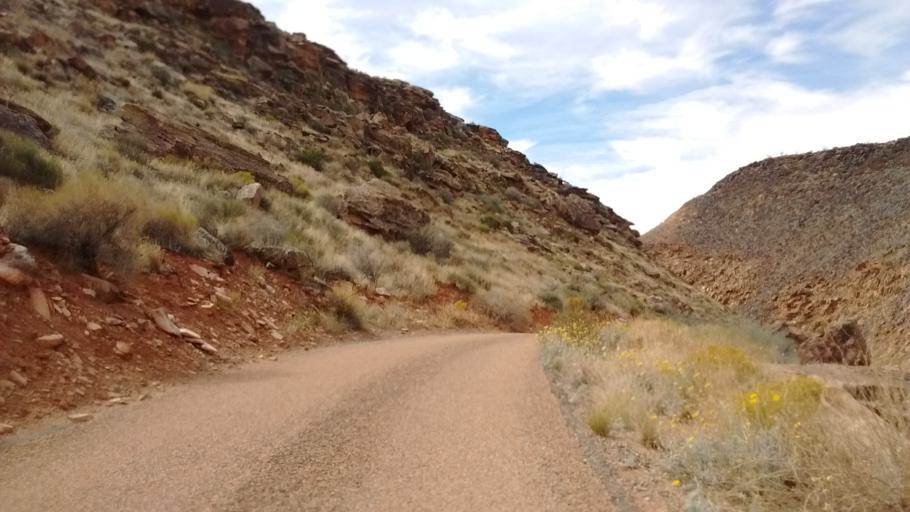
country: US
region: Utah
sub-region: Washington County
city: Washington
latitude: 37.1277
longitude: -113.4753
